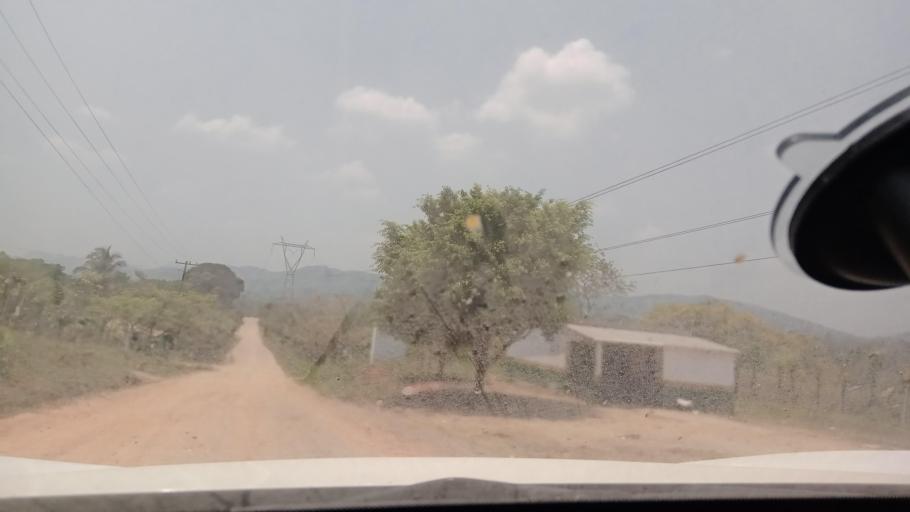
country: MX
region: Chiapas
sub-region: Tecpatan
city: Raudales Malpaso
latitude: 17.4517
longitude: -93.7926
